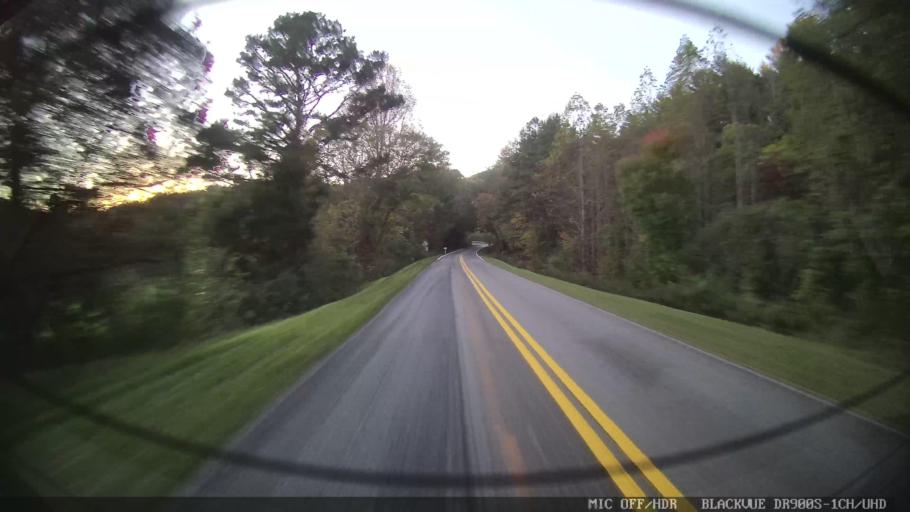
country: US
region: Georgia
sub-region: Union County
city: Blairsville
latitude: 34.8549
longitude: -83.9012
